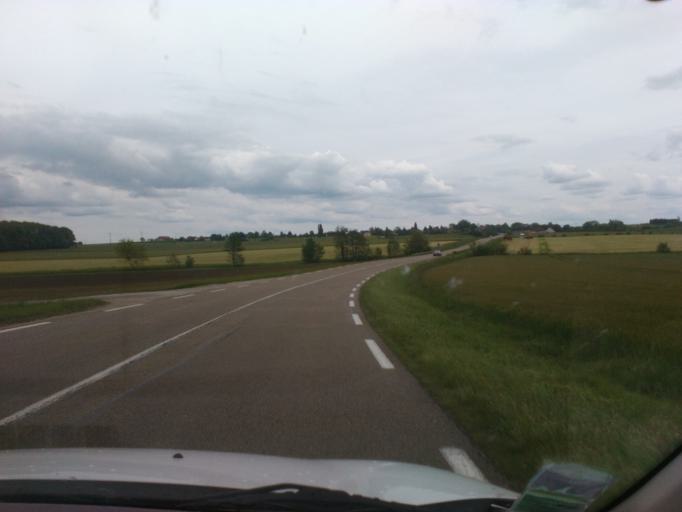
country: FR
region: Champagne-Ardenne
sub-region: Departement de l'Aube
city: Vendeuvre-sur-Barse
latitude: 48.2418
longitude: 4.3713
